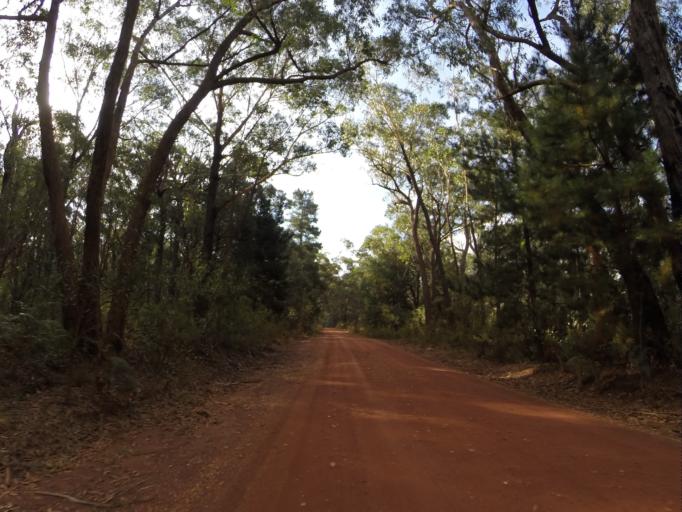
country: AU
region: New South Wales
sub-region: Wingecarribee
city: Bundanoon
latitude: -34.5264
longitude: 150.2132
